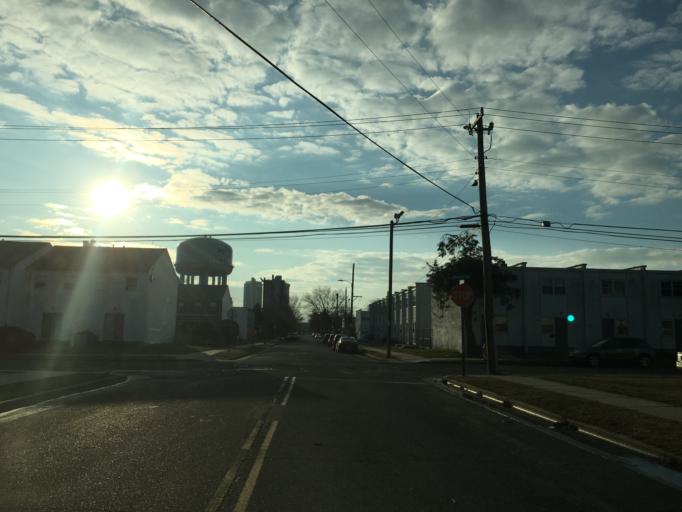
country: US
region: New Jersey
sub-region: Atlantic County
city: Atlantic City
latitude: 39.3725
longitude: -74.4286
